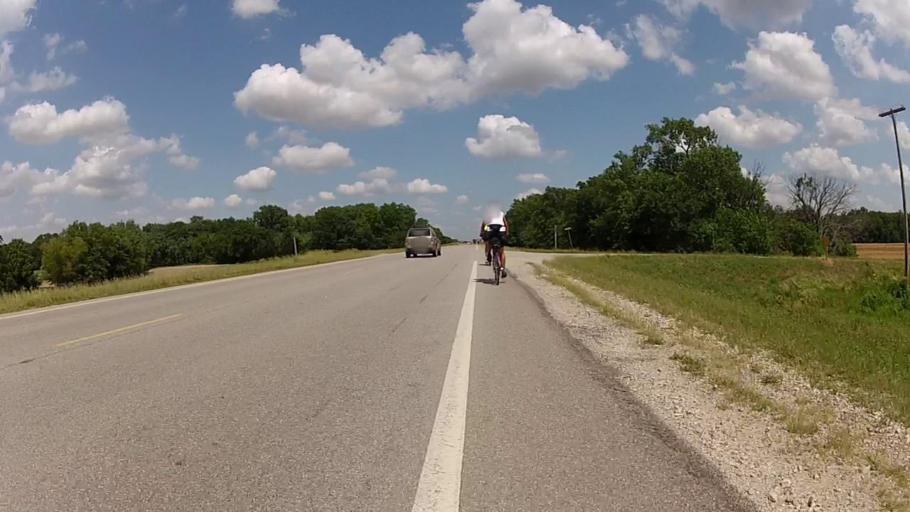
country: US
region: Kansas
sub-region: Labette County
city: Oswego
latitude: 37.1938
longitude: -95.1950
